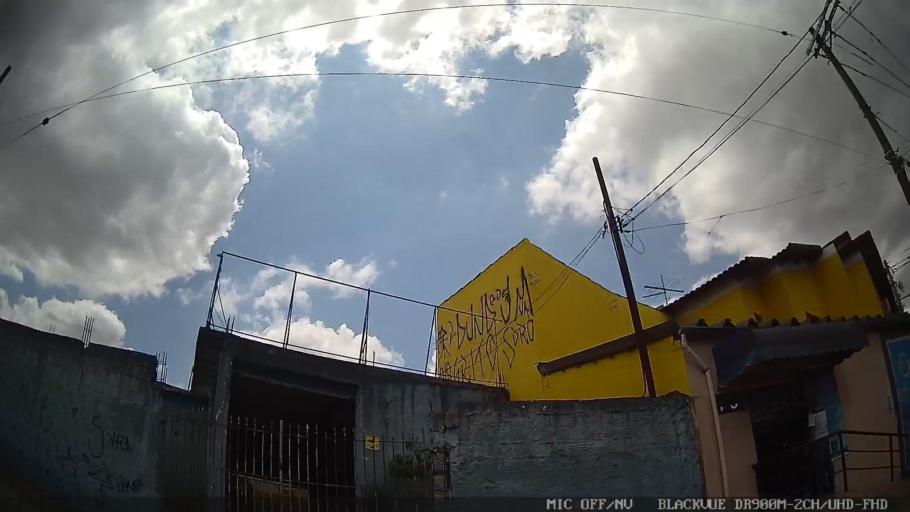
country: BR
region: Sao Paulo
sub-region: Ferraz De Vasconcelos
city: Ferraz de Vasconcelos
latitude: -23.5325
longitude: -46.4613
